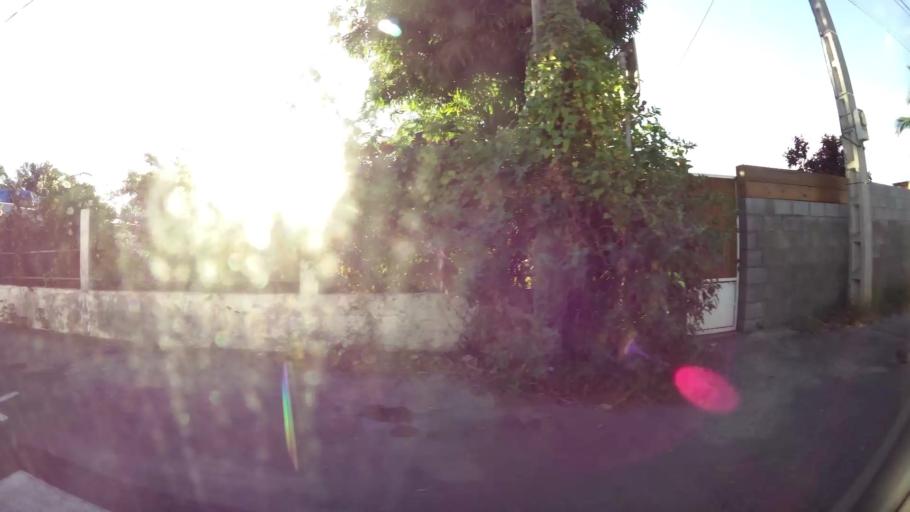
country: RE
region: Reunion
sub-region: Reunion
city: Trois-Bassins
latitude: -21.0950
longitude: 55.2380
